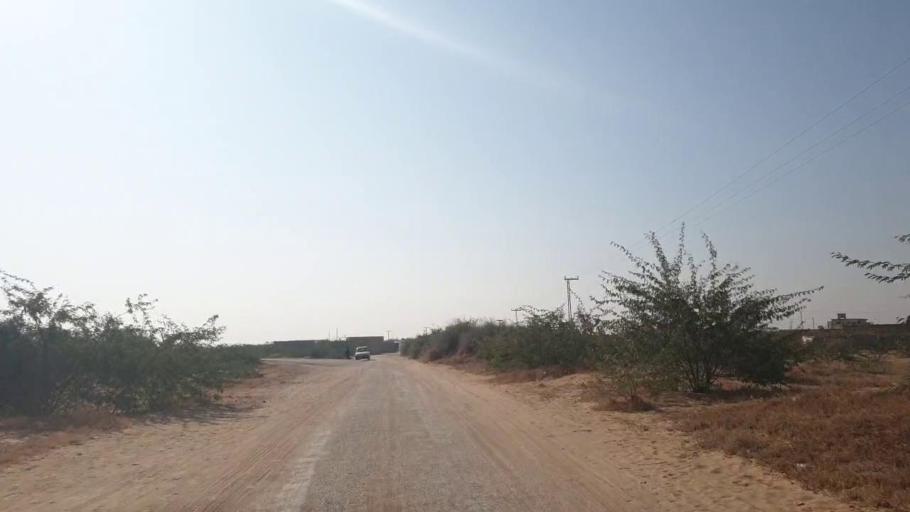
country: PK
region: Sindh
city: Thatta
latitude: 25.1359
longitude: 67.7721
